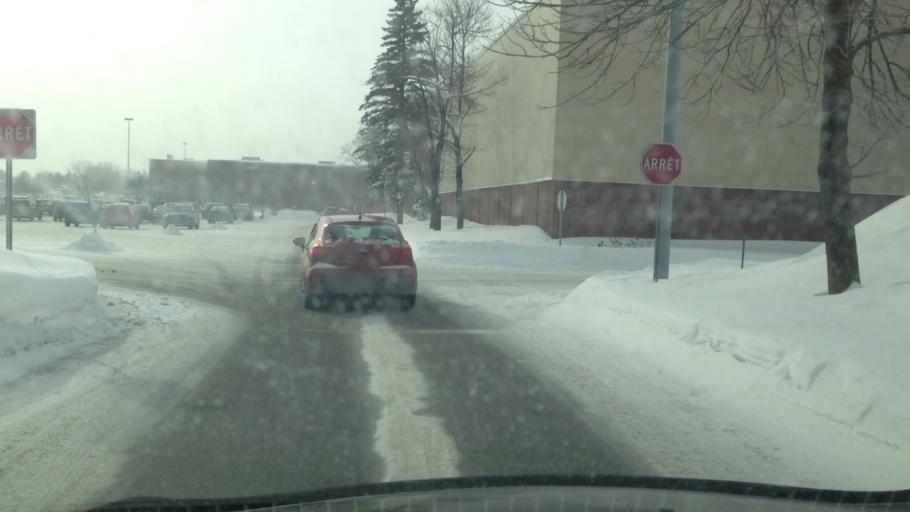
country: CA
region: Quebec
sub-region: Laurentides
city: Saint-Jerome
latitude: 45.7963
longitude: -74.0172
